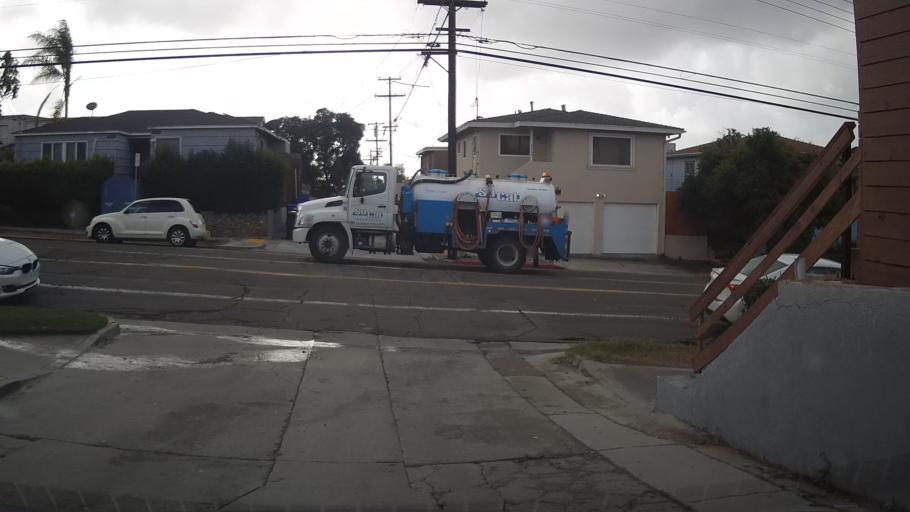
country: US
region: California
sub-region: San Diego County
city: San Diego
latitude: 32.7481
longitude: -117.1187
